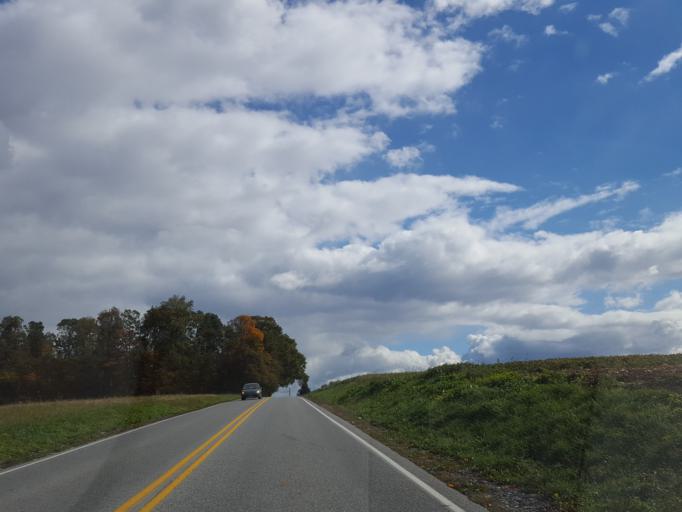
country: US
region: Pennsylvania
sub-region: York County
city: Yoe
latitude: 39.9217
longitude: -76.6393
